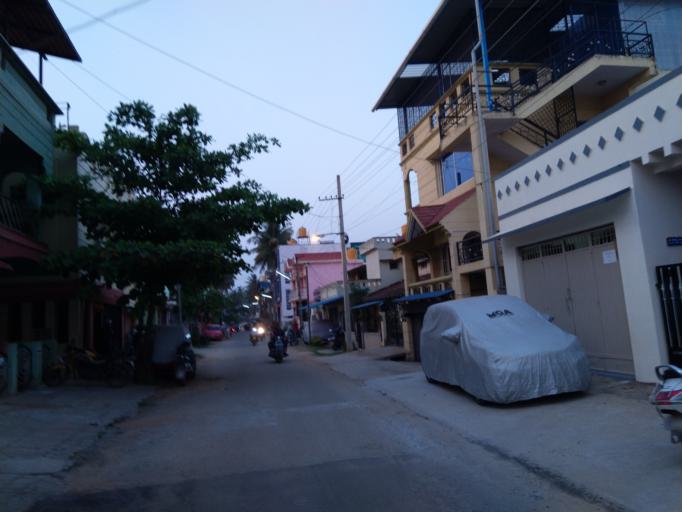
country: IN
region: Karnataka
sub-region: Hassan
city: Hassan
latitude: 13.0108
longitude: 76.1090
